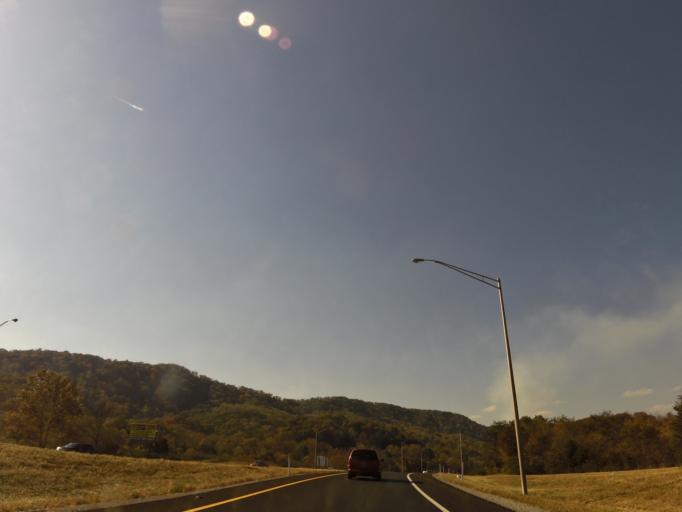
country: US
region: Tennessee
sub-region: Anderson County
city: Rocky Top
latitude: 36.2349
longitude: -84.1629
